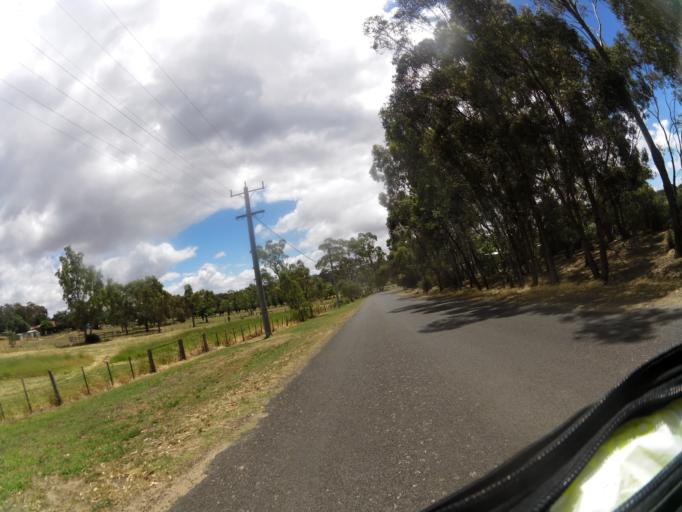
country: AU
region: Victoria
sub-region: Mount Alexander
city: Castlemaine
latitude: -37.0144
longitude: 144.2515
